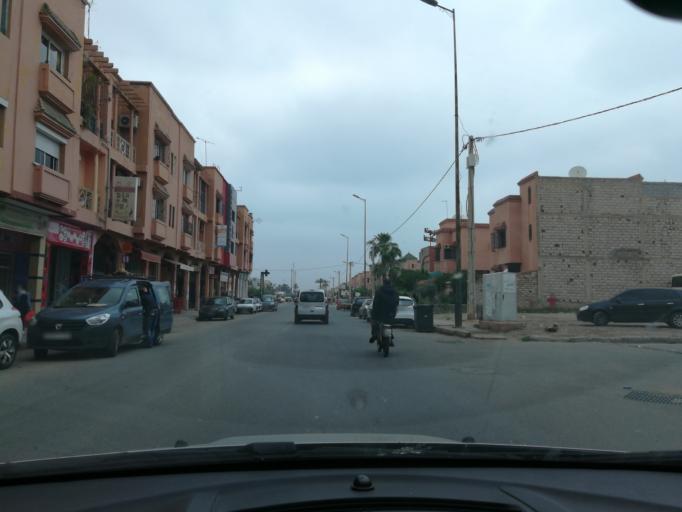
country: MA
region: Marrakech-Tensift-Al Haouz
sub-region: Marrakech
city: Marrakesh
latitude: 31.6620
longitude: -7.9930
